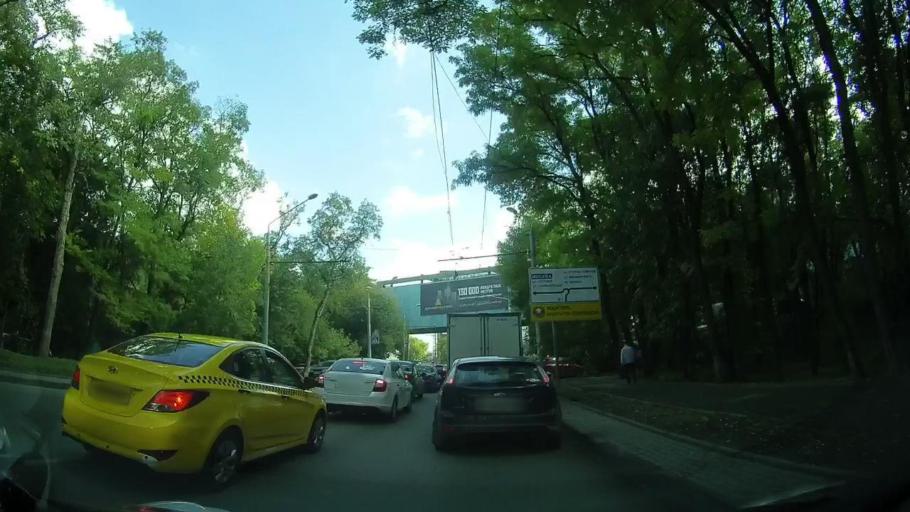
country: RU
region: Rostov
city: Imeni Chkalova
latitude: 47.2725
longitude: 39.7606
